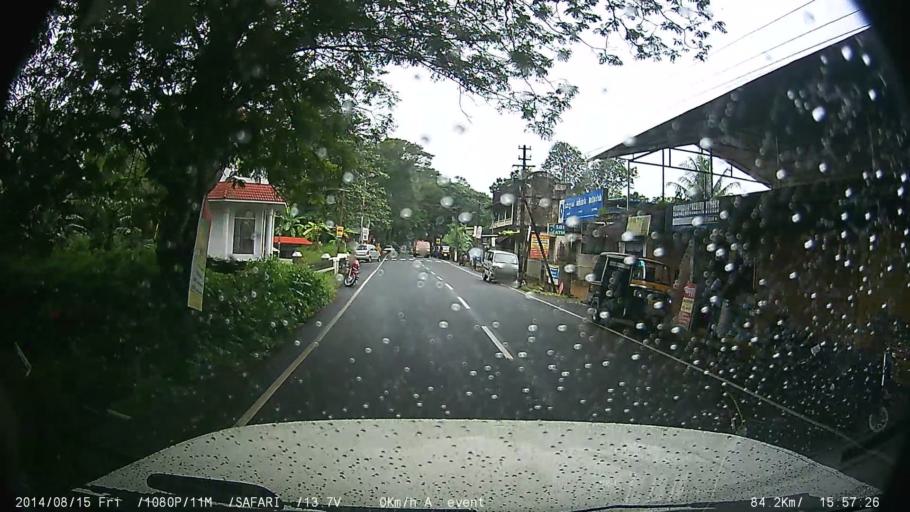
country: IN
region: Kerala
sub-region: Kottayam
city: Lalam
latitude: 9.7788
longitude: 76.7298
